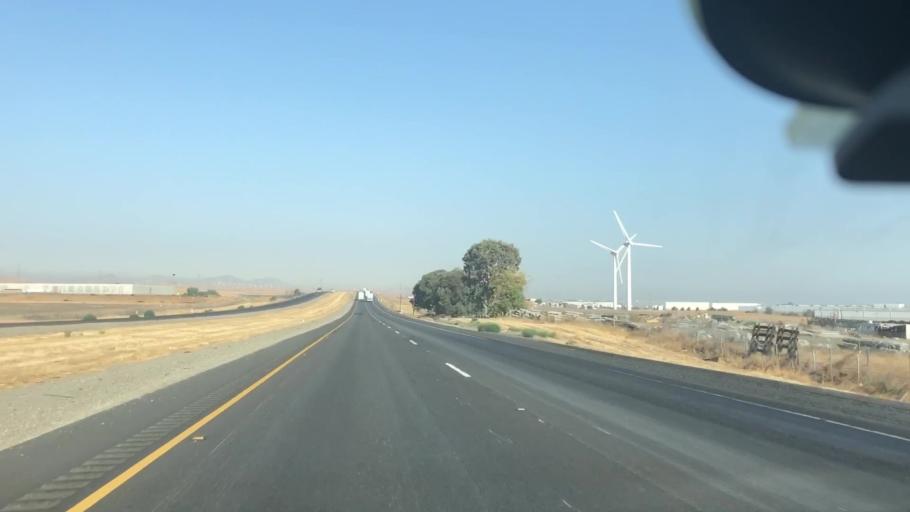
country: US
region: California
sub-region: San Joaquin County
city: Mountain House
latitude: 37.7082
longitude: -121.5164
